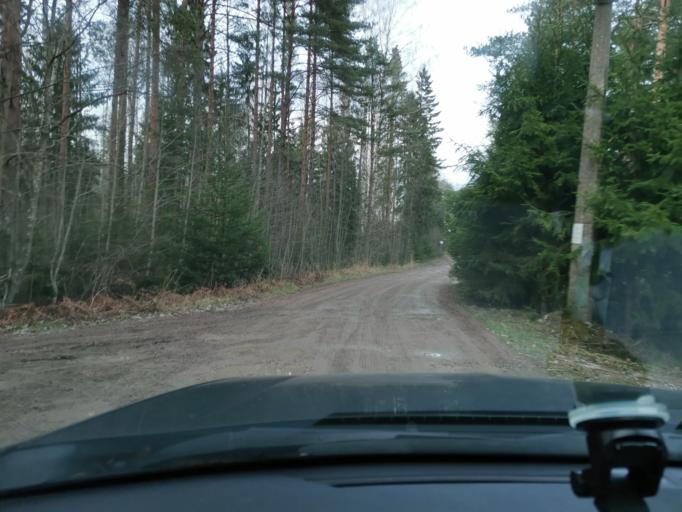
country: EE
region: Ida-Virumaa
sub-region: Sillamaee linn
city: Sillamae
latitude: 59.2538
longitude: 27.9137
